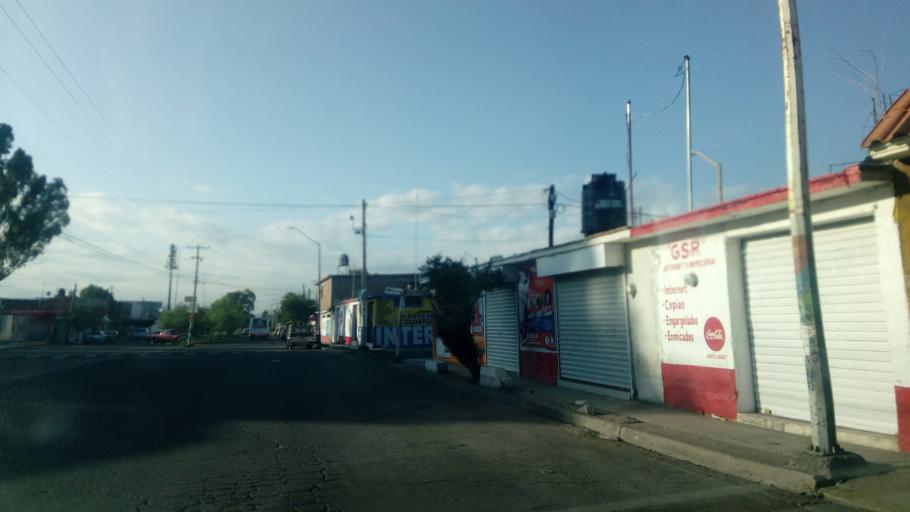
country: MX
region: Durango
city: Victoria de Durango
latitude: 24.0463
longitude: -104.6147
